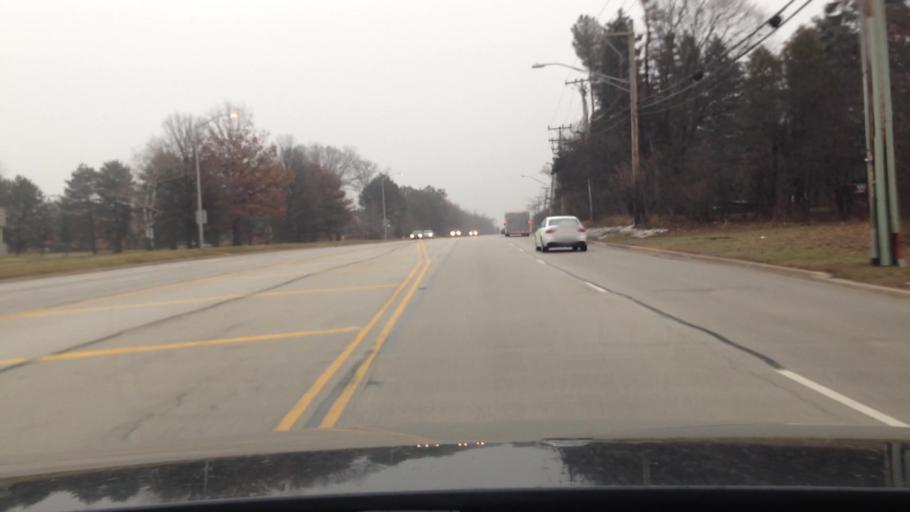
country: US
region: Illinois
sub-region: DuPage County
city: Downers Grove
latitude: 41.8311
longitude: -88.0053
